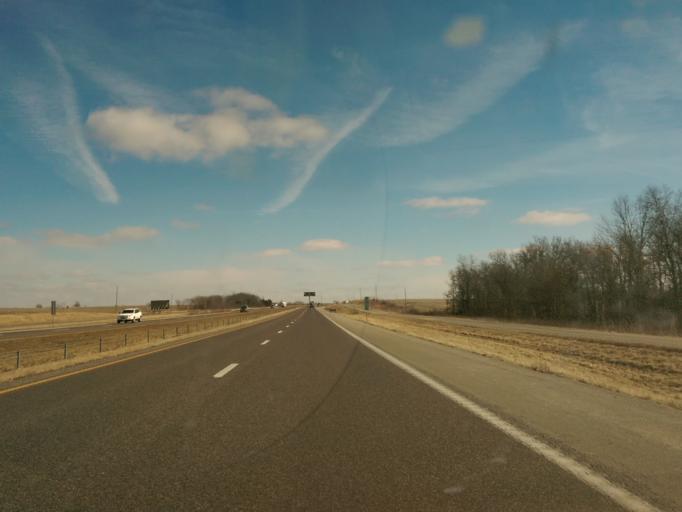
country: US
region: Missouri
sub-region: Callaway County
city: Fulton
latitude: 38.9436
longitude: -91.8875
